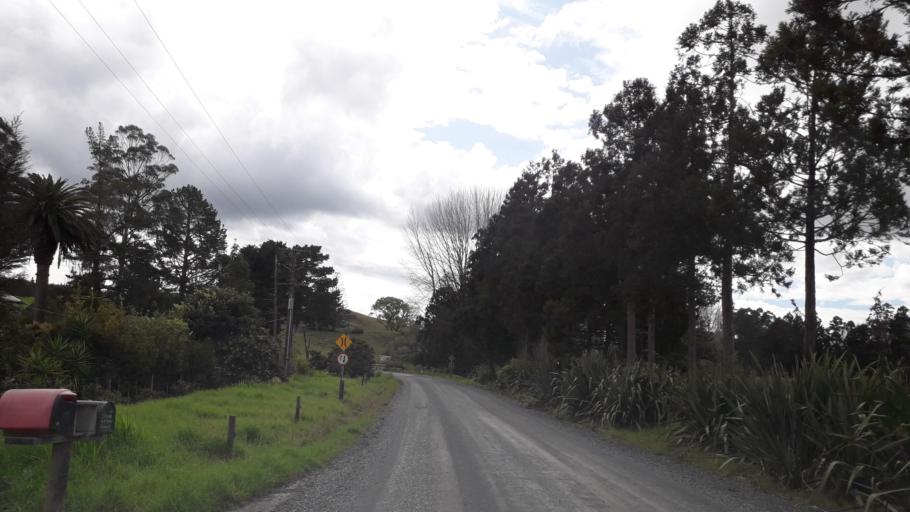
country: NZ
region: Northland
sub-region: Far North District
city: Taipa
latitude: -35.0866
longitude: 173.5113
